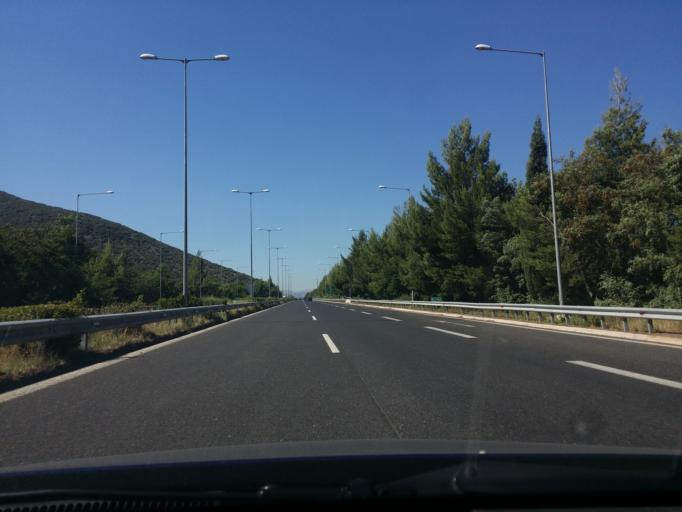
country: GR
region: Peloponnese
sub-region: Nomos Arkadias
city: Tripoli
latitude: 37.5786
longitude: 22.4308
